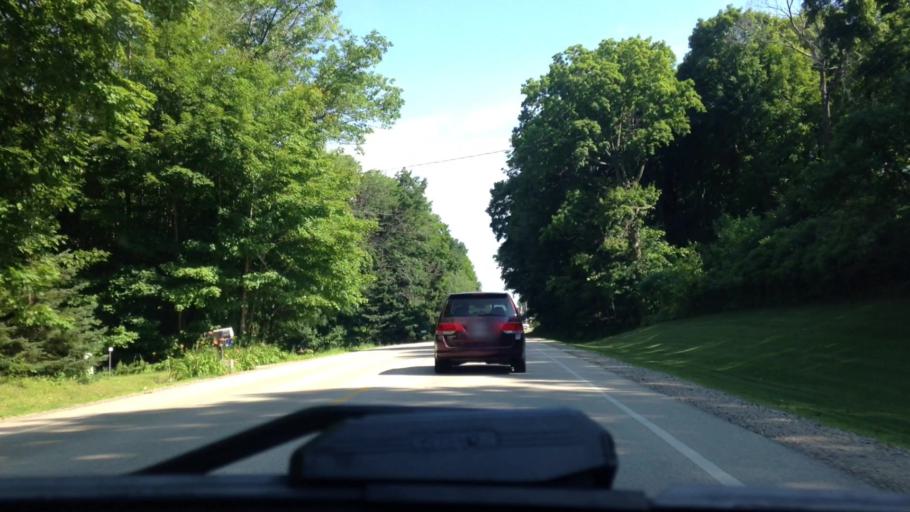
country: US
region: Wisconsin
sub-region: Washington County
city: West Bend
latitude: 43.3988
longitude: -88.2410
